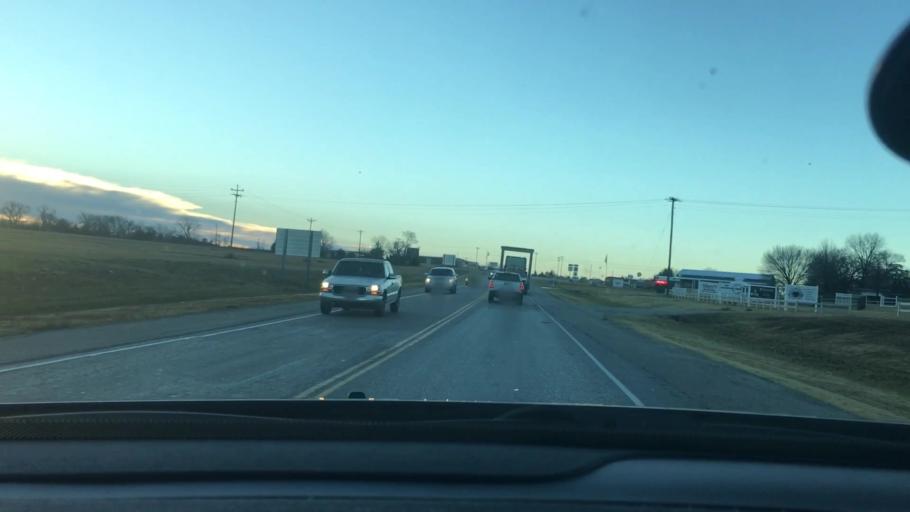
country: US
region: Oklahoma
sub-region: Pontotoc County
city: Ada
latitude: 34.7577
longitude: -96.7031
